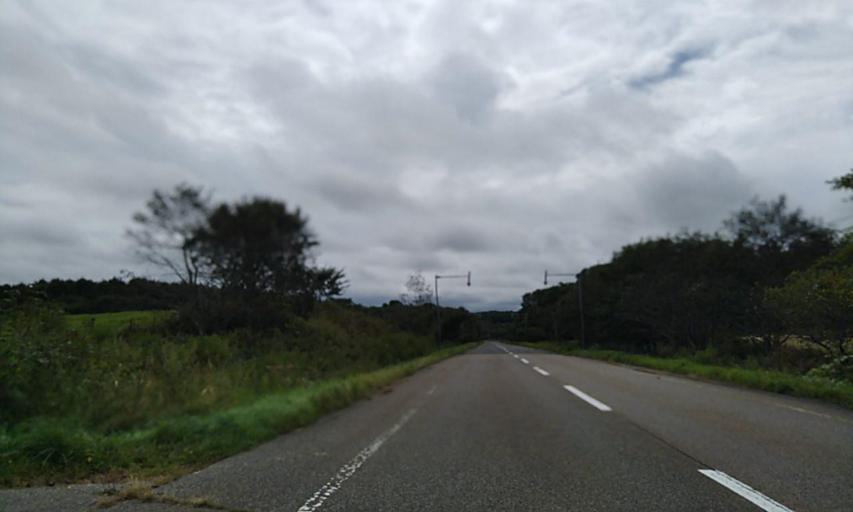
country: JP
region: Hokkaido
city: Shibetsu
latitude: 43.3328
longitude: 145.2151
